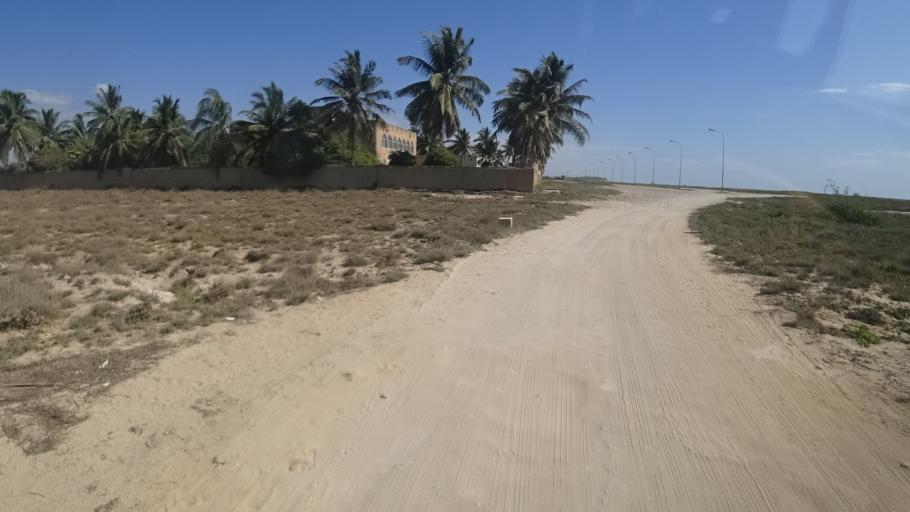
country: OM
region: Zufar
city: Salalah
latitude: 16.9940
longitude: 54.0587
